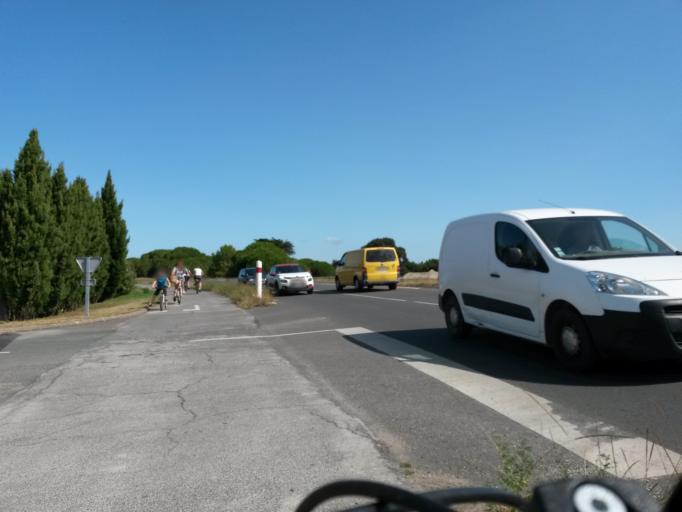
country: FR
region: Poitou-Charentes
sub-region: Departement de la Charente-Maritime
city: Saint-Martin-de-Re
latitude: 46.1893
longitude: -1.3679
